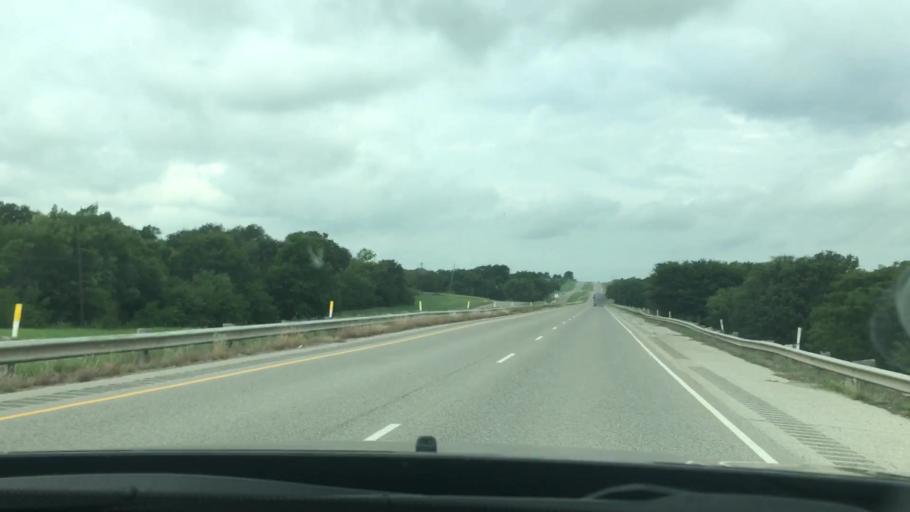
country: US
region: Oklahoma
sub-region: Carter County
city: Wilson
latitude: 34.1731
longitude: -97.4471
